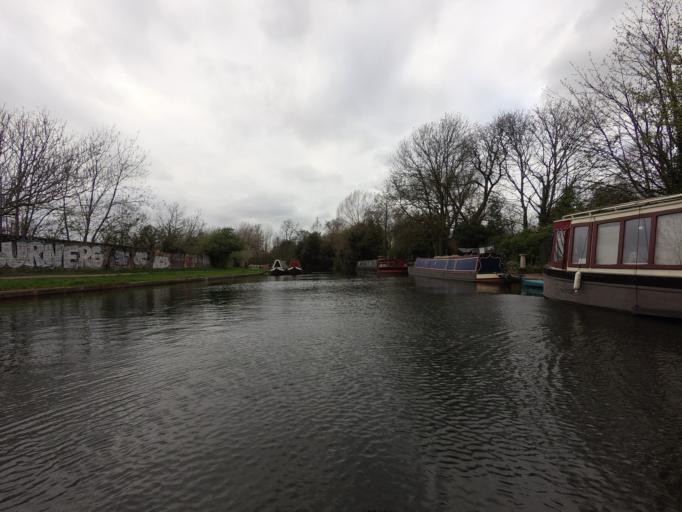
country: GB
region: England
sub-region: Greater London
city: Hammersmith
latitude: 51.5272
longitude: -0.2185
